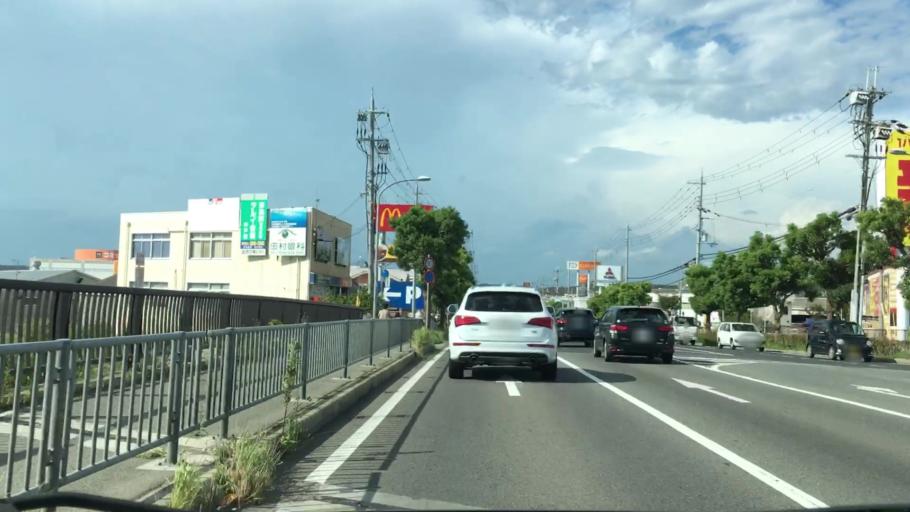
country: JP
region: Hyogo
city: Akashi
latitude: 34.6782
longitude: 134.9820
